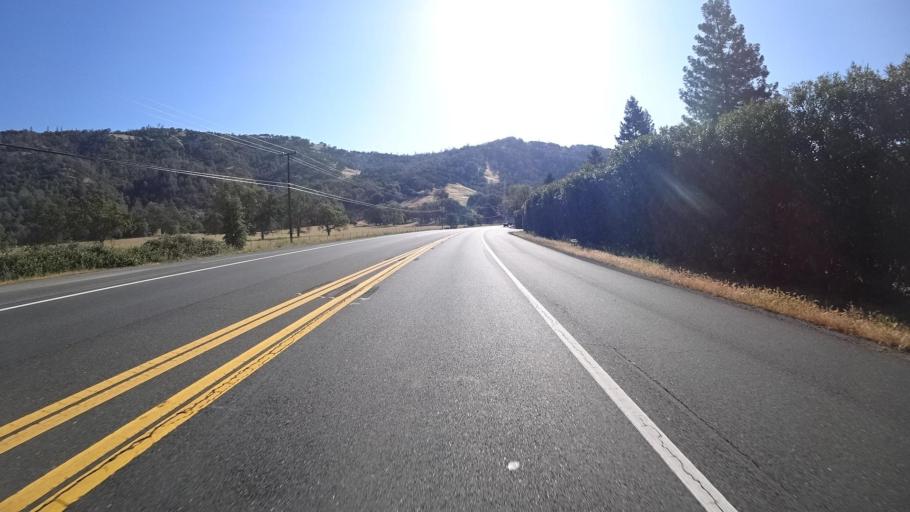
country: US
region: California
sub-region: Lake County
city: Soda Bay
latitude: 39.0429
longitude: -122.7547
